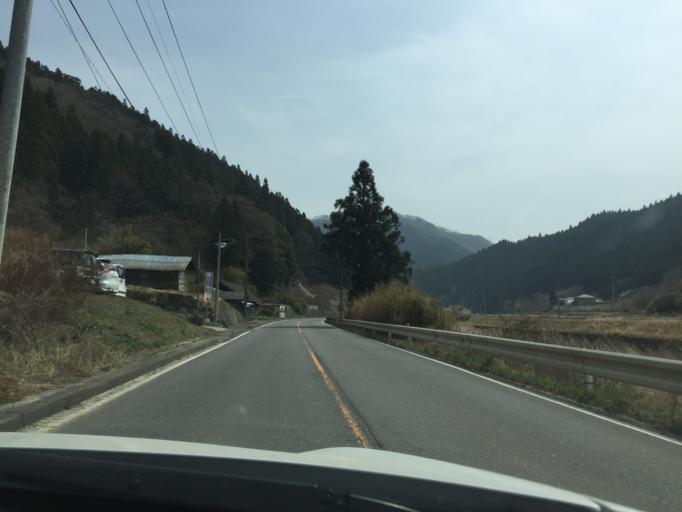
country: JP
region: Fukushima
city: Ishikawa
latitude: 37.0640
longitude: 140.5839
